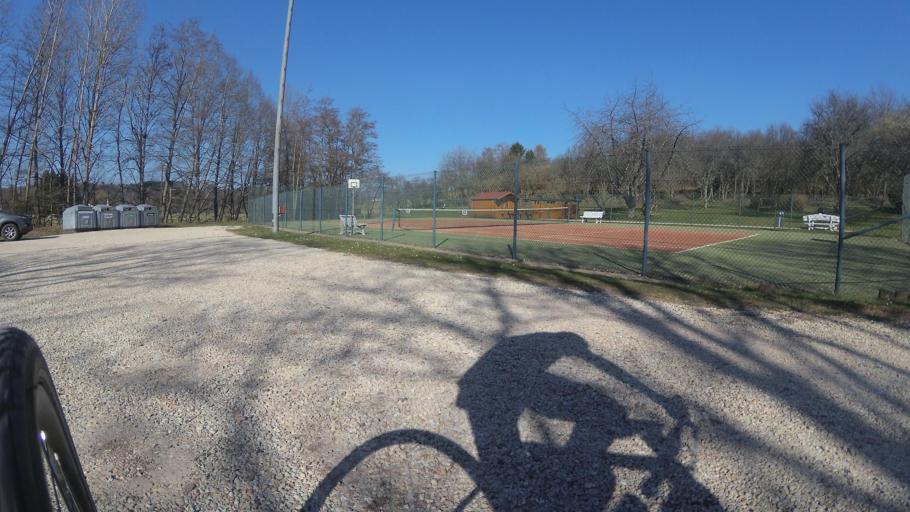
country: DE
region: Rheinland-Pfalz
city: Achtelsbach
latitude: 49.5693
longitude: 7.0591
